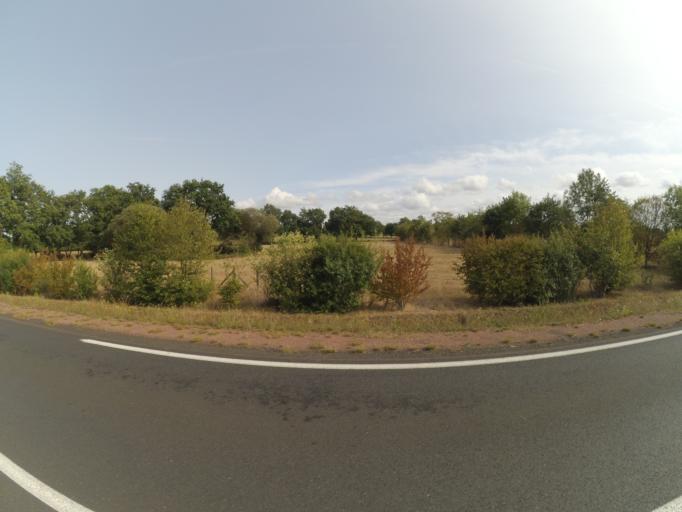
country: FR
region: Pays de la Loire
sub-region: Departement de la Vendee
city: Treize-Septiers
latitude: 46.9854
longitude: -1.2006
